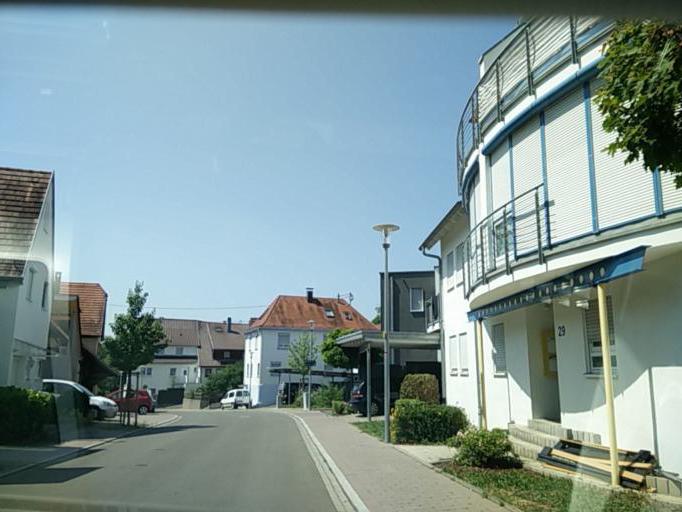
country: DE
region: Baden-Wuerttemberg
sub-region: Tuebingen Region
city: Gomaringen
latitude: 48.4552
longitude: 9.1020
